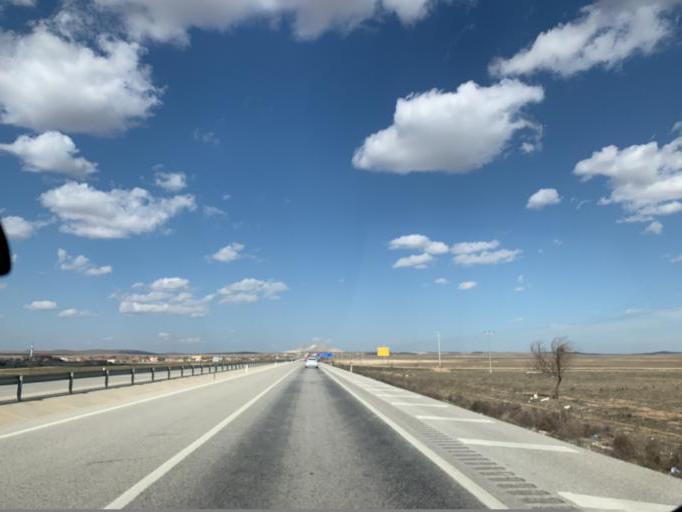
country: TR
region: Konya
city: Cihanbeyli
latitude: 38.5052
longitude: 32.8493
